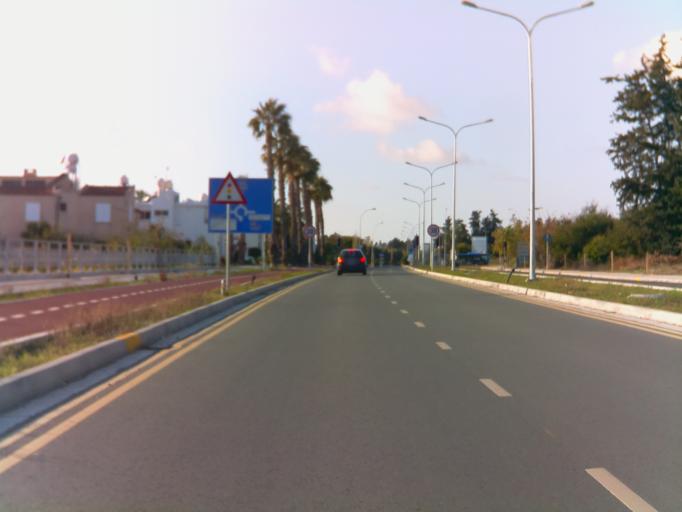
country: CY
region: Pafos
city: Paphos
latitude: 34.7505
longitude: 32.4311
